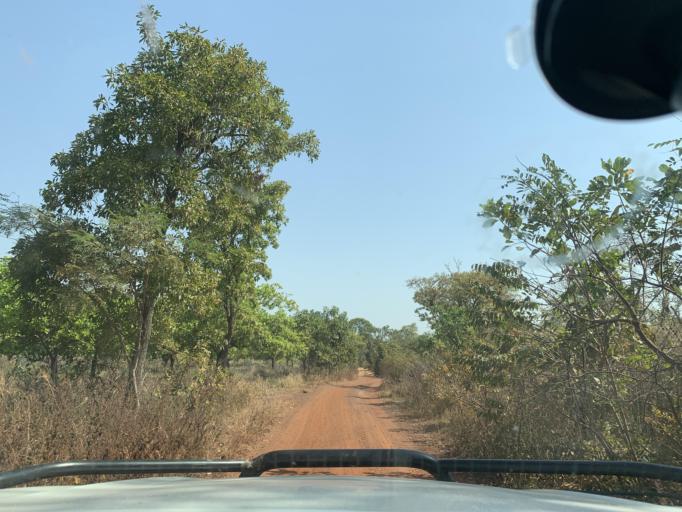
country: ML
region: Sikasso
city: Kolondieba
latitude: 10.8913
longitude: -6.7548
